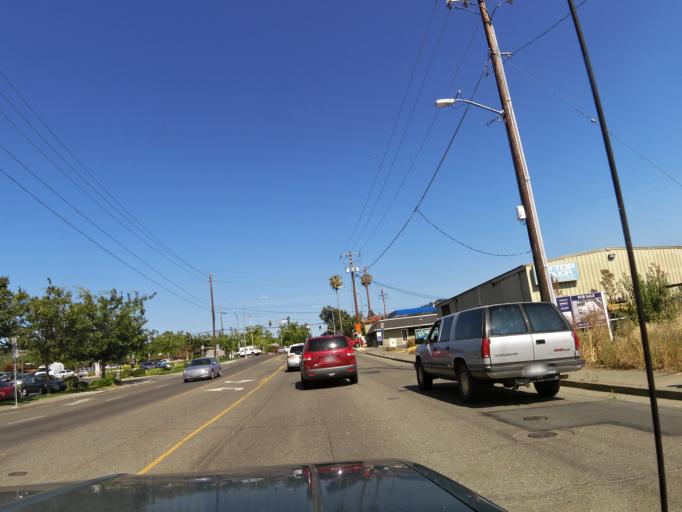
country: US
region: California
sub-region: Sonoma County
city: Healdsburg
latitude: 38.6262
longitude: -122.8741
